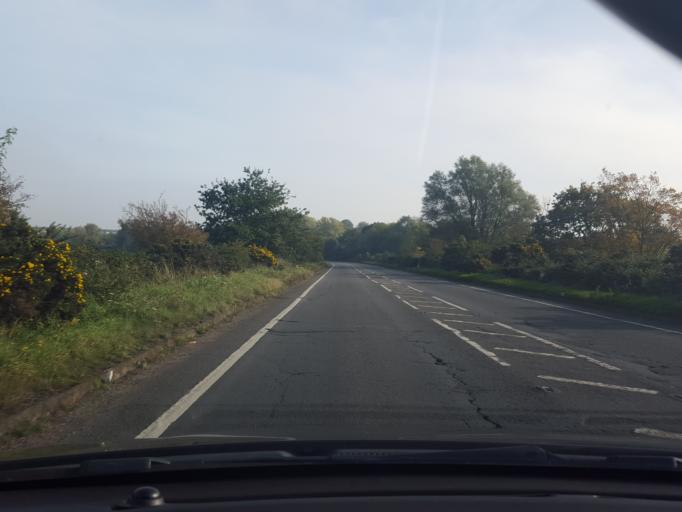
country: GB
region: England
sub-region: Suffolk
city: Shotley Gate
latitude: 51.9347
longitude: 1.2407
